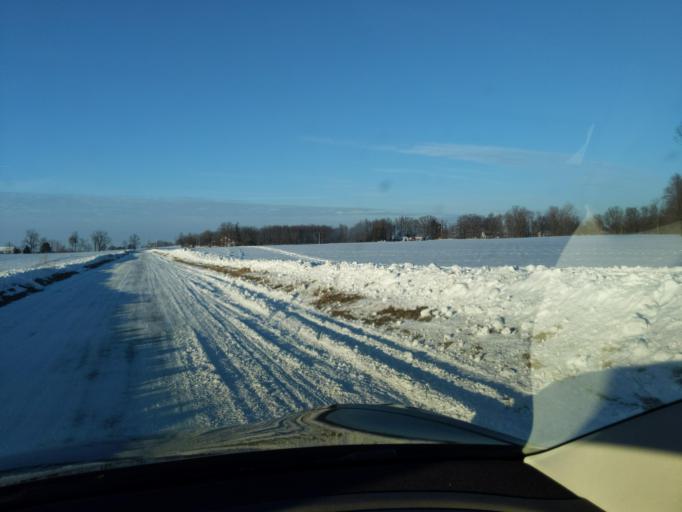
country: US
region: Michigan
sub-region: Ingham County
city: Stockbridge
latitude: 42.4924
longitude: -84.1195
